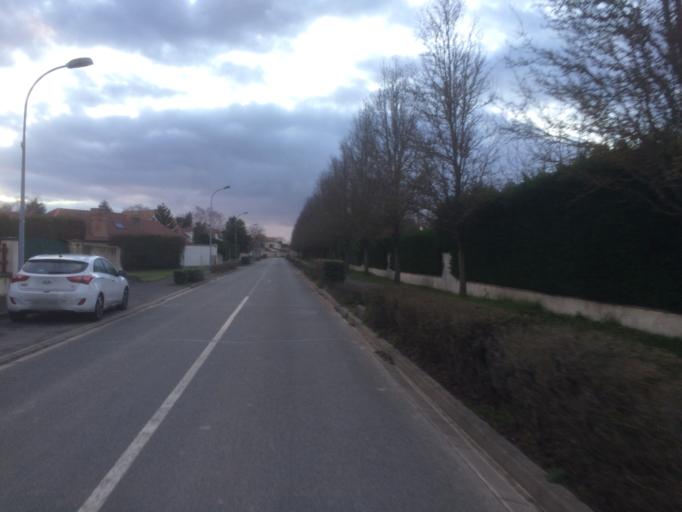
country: FR
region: Ile-de-France
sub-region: Departement de l'Essonne
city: Villejust
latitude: 48.6731
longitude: 2.2172
